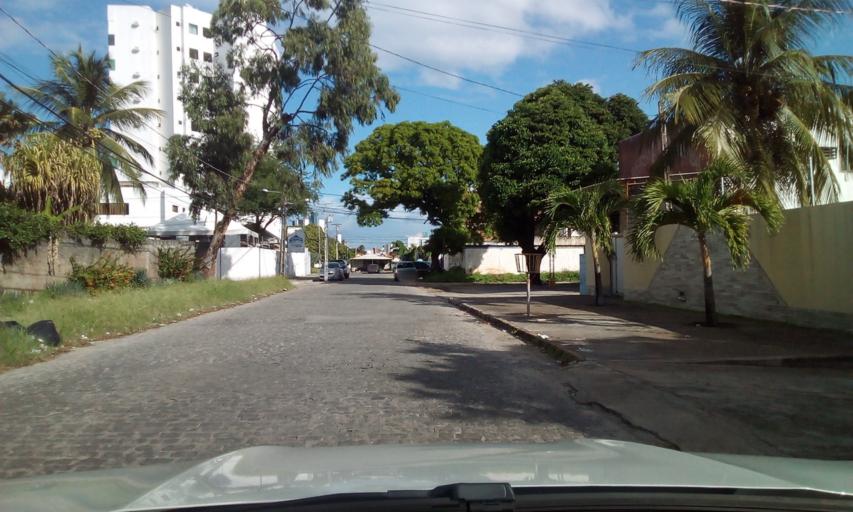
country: BR
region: Paraiba
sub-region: Joao Pessoa
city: Joao Pessoa
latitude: -7.0751
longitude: -34.8361
